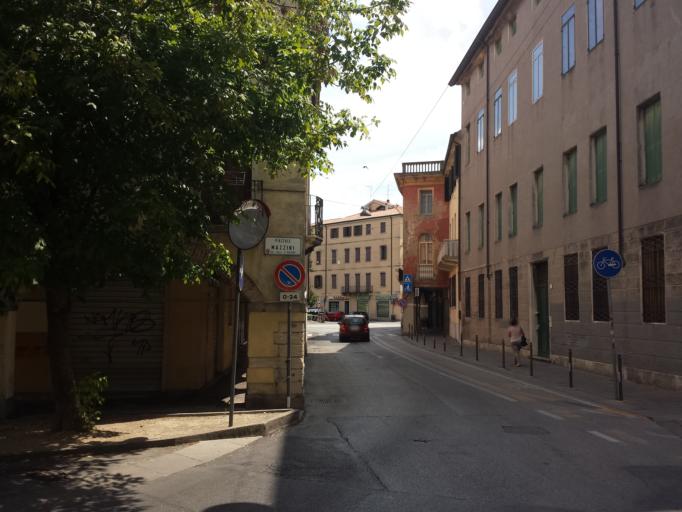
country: IT
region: Veneto
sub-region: Provincia di Padova
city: Padova
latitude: 45.4131
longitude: 11.8732
